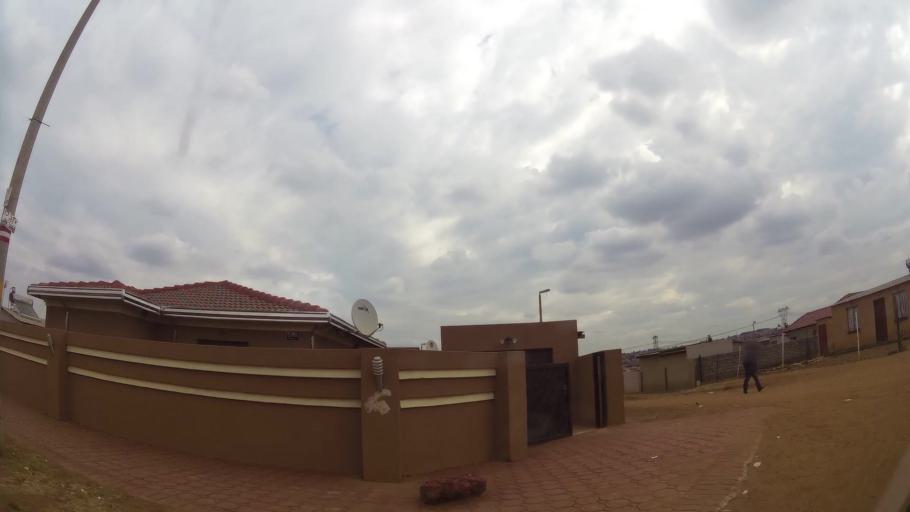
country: ZA
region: Gauteng
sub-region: Ekurhuleni Metropolitan Municipality
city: Germiston
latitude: -26.3732
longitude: 28.1186
